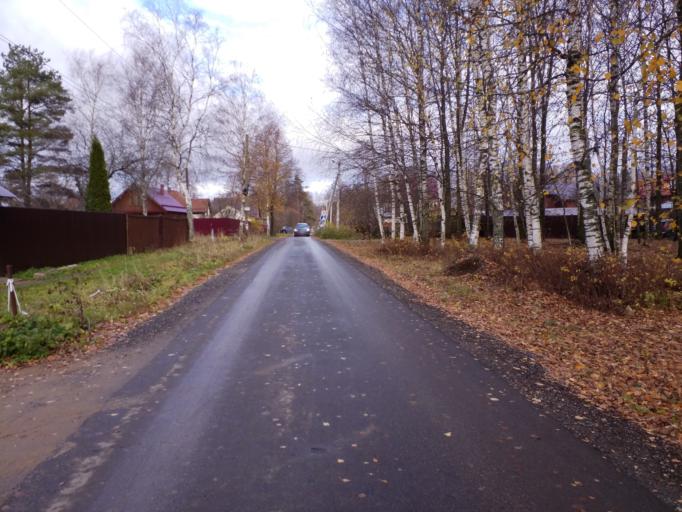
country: RU
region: Moskovskaya
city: Ashukino
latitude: 56.1634
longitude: 37.9372
